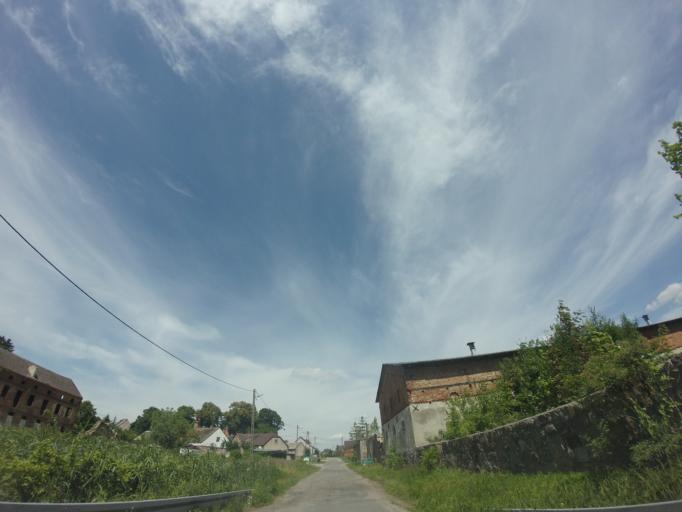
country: PL
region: West Pomeranian Voivodeship
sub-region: Powiat choszczenski
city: Recz
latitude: 53.3438
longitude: 15.5425
